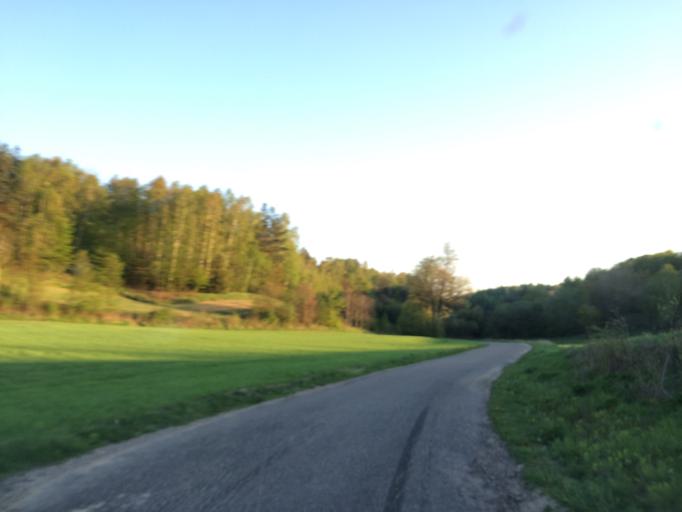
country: PL
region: Warmian-Masurian Voivodeship
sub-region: Powiat ilawski
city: Lubawa
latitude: 53.5198
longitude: 19.8773
